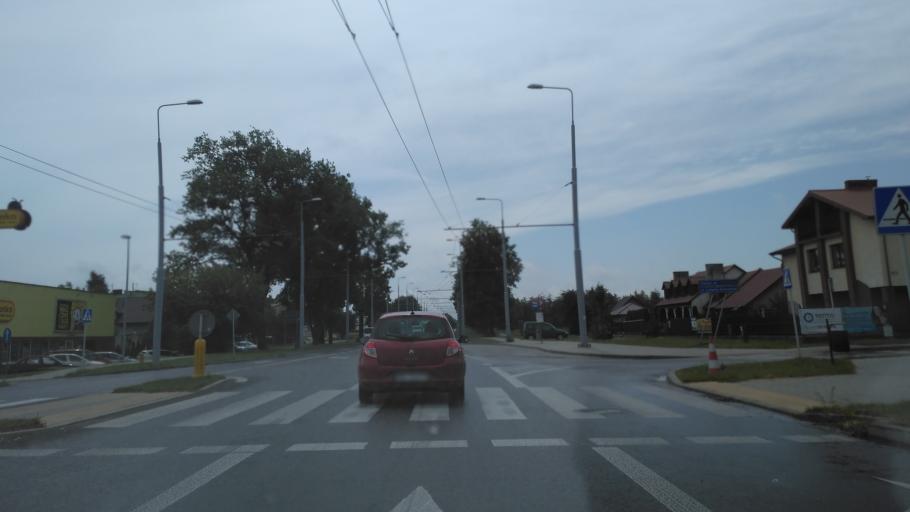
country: PL
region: Lublin Voivodeship
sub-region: Powiat lubelski
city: Lublin
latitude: 51.2010
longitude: 22.5859
